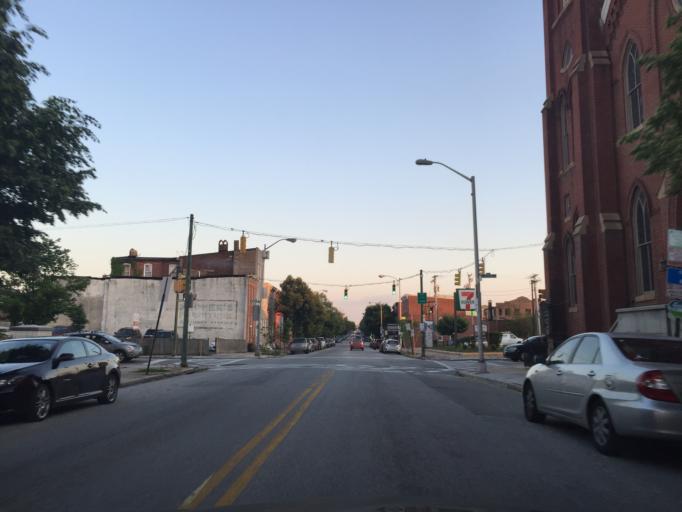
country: US
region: Maryland
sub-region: City of Baltimore
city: Baltimore
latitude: 39.2781
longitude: -76.6156
